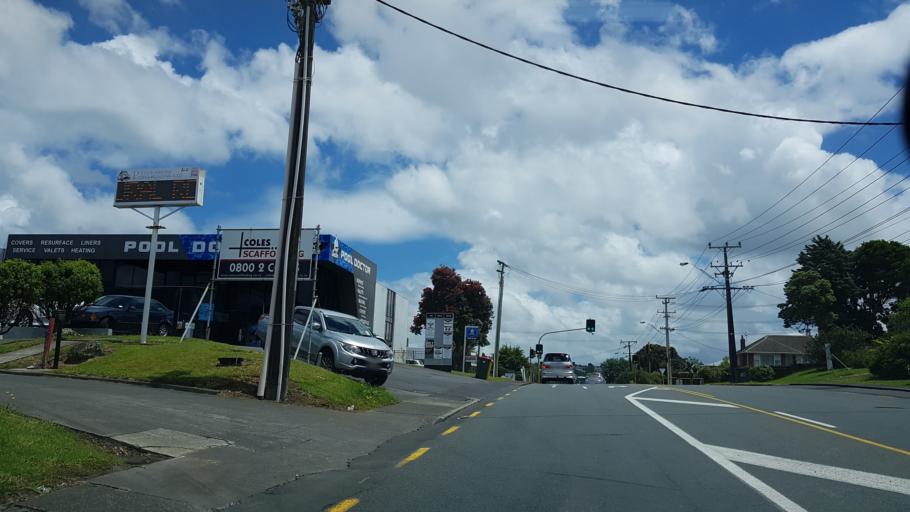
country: NZ
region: Auckland
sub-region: Auckland
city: North Shore
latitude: -36.7817
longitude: 174.7383
